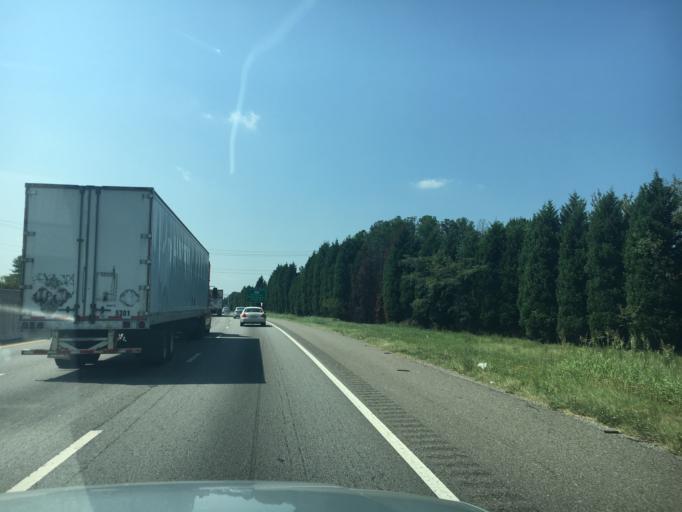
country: US
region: South Carolina
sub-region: Greenville County
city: Mauldin
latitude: 34.8112
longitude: -82.3432
